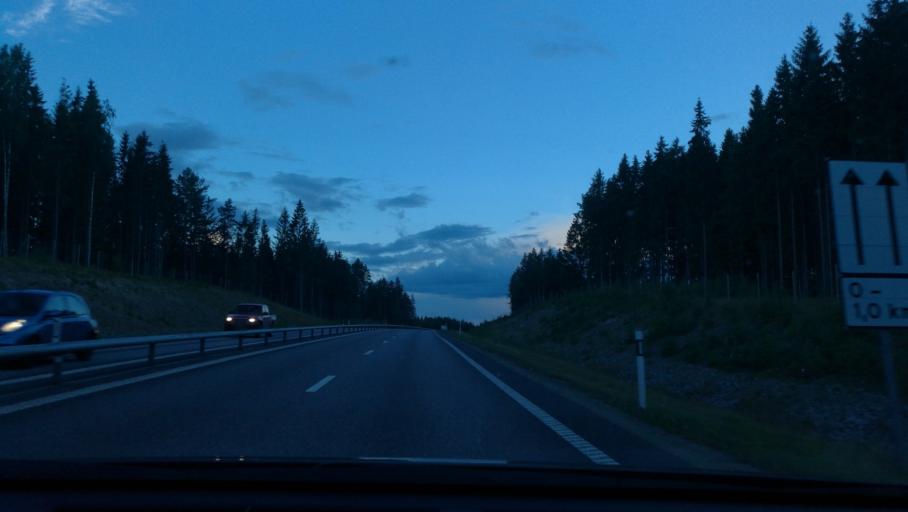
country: SE
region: Soedermanland
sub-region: Katrineholms Kommun
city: Katrineholm
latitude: 58.9680
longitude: 16.2561
